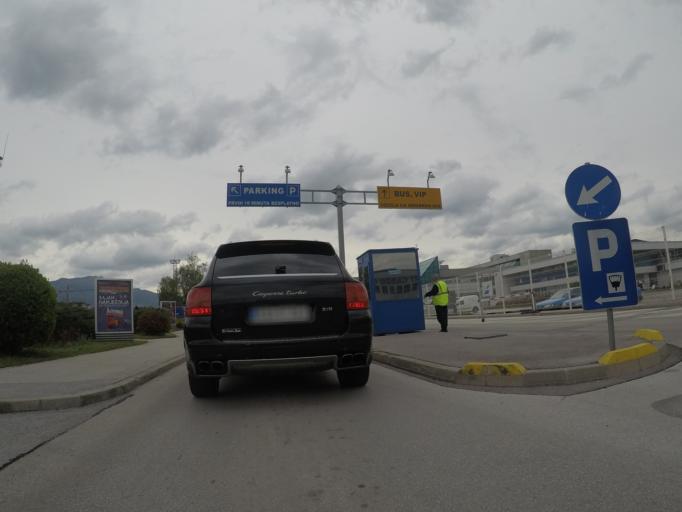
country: BA
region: Federation of Bosnia and Herzegovina
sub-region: Kanton Sarajevo
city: Sarajevo
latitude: 43.8270
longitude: 18.3356
